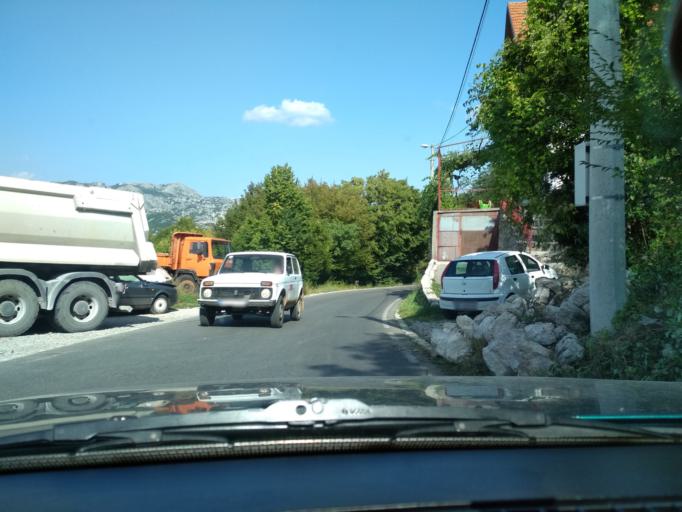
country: ME
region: Cetinje
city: Cetinje
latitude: 42.3901
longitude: 18.9026
